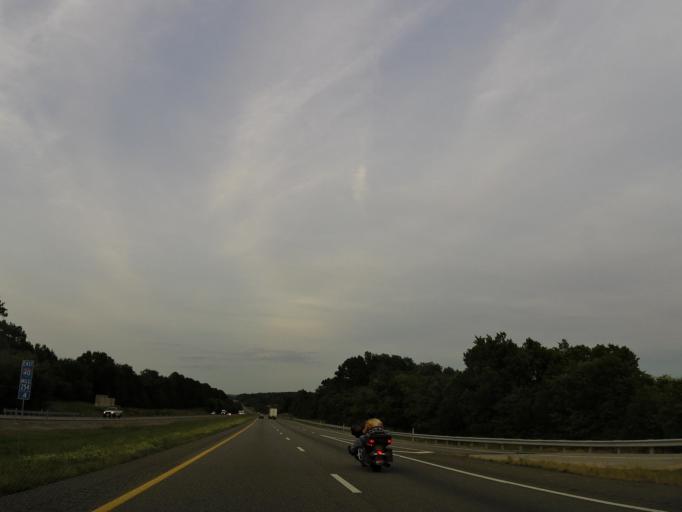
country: US
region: Tennessee
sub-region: Smith County
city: Gordonsville
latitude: 36.1755
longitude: -86.0174
